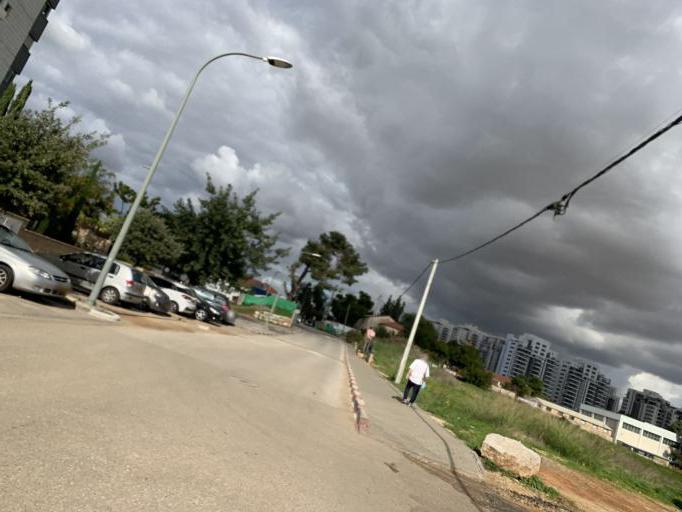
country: IL
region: Central District
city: Hod HaSharon
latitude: 32.1610
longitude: 34.8961
